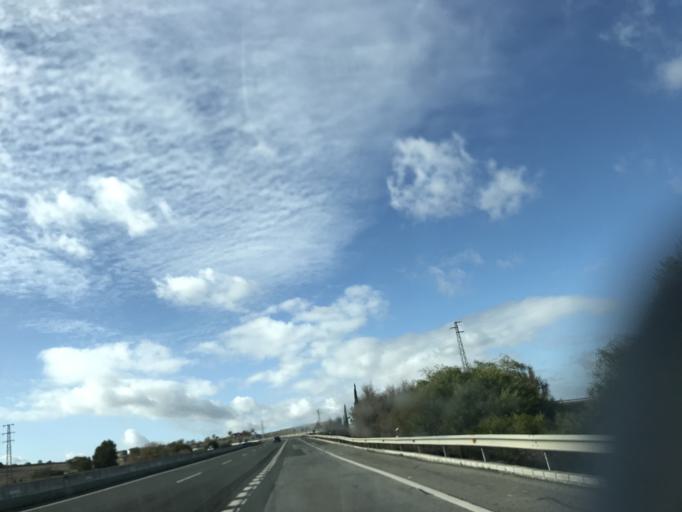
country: ES
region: Andalusia
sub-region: Provincia de Sevilla
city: Ecija
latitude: 37.5299
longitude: -5.0868
